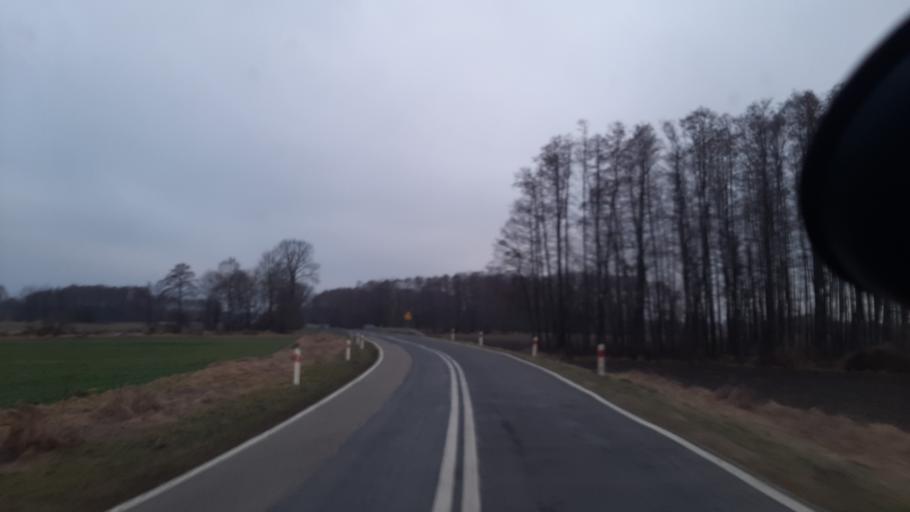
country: PL
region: Lublin Voivodeship
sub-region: Powiat parczewski
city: Podedworze
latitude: 51.5930
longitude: 23.1789
